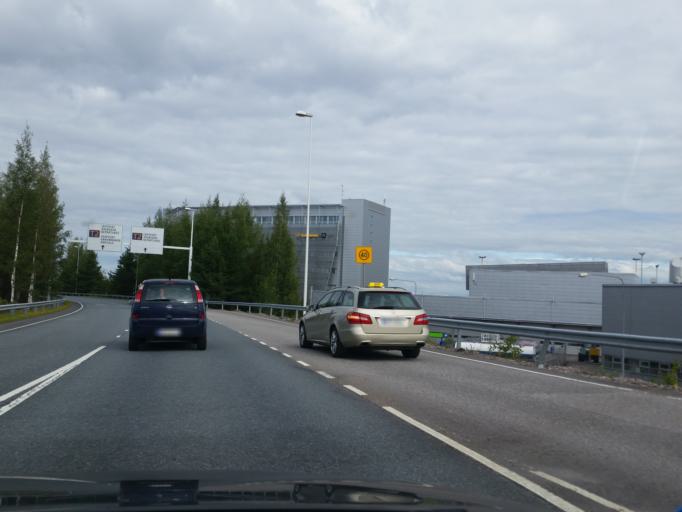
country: FI
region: Uusimaa
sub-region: Helsinki
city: Vantaa
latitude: 60.3125
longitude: 24.9720
